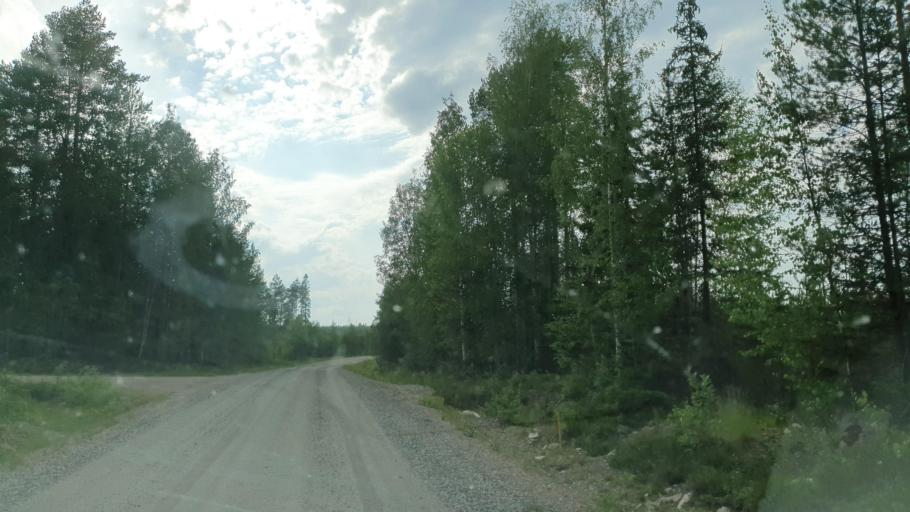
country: FI
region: Kainuu
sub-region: Kehys-Kainuu
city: Kuhmo
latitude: 64.0537
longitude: 29.7820
